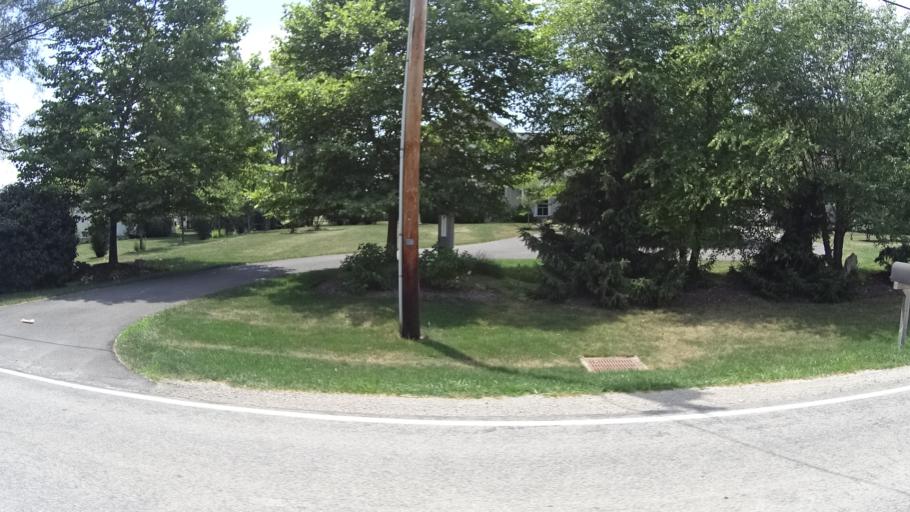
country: US
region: Ohio
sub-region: Erie County
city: Sandusky
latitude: 41.3909
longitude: -82.7708
